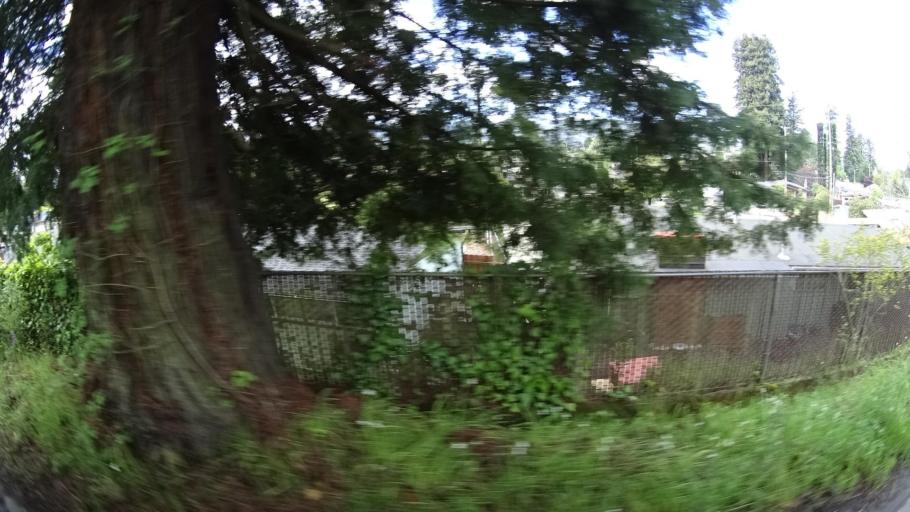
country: US
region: California
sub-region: Humboldt County
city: Blue Lake
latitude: 40.8821
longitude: -123.9797
